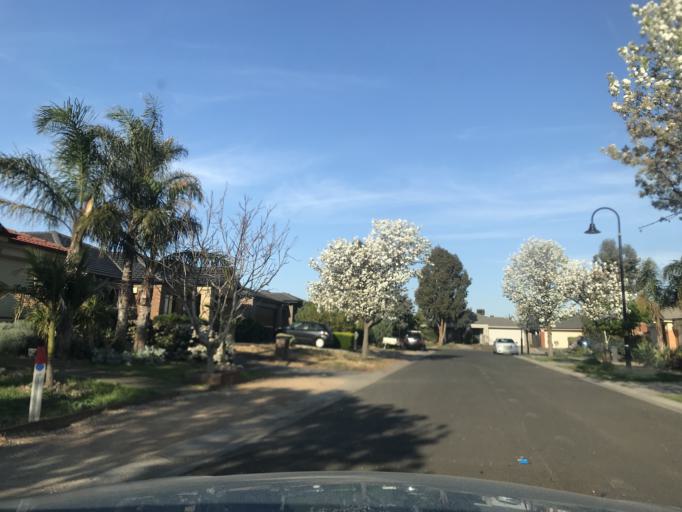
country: AU
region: Victoria
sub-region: Wyndham
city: Williams Landing
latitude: -37.8582
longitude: 144.7213
